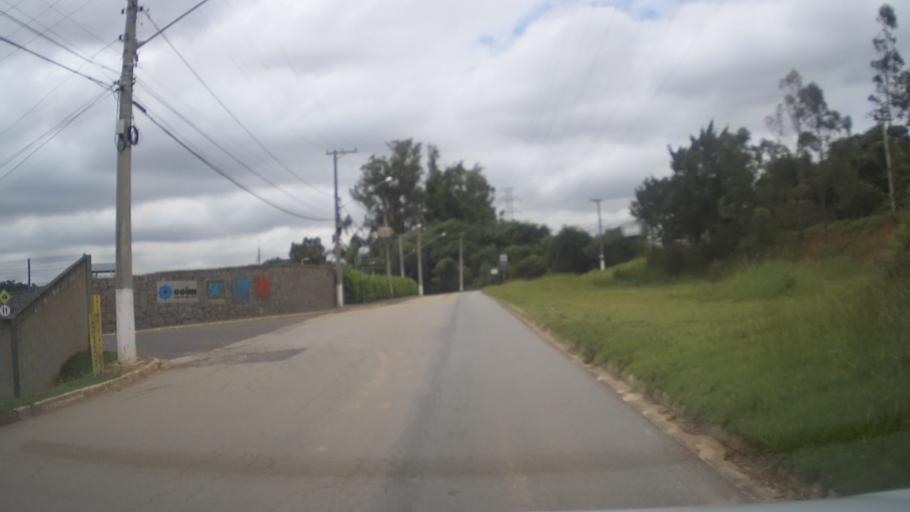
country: BR
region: Sao Paulo
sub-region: Louveira
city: Louveira
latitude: -23.0736
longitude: -46.9897
